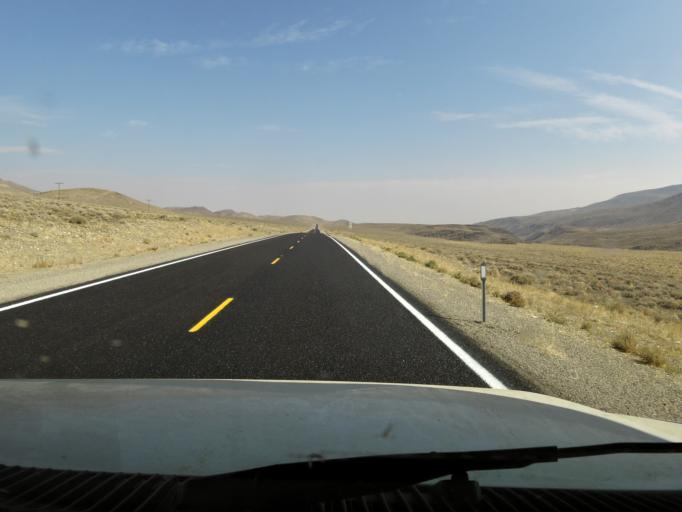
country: US
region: California
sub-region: Inyo County
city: Dixon Lane-Meadow Creek
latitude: 38.0055
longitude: -118.1526
